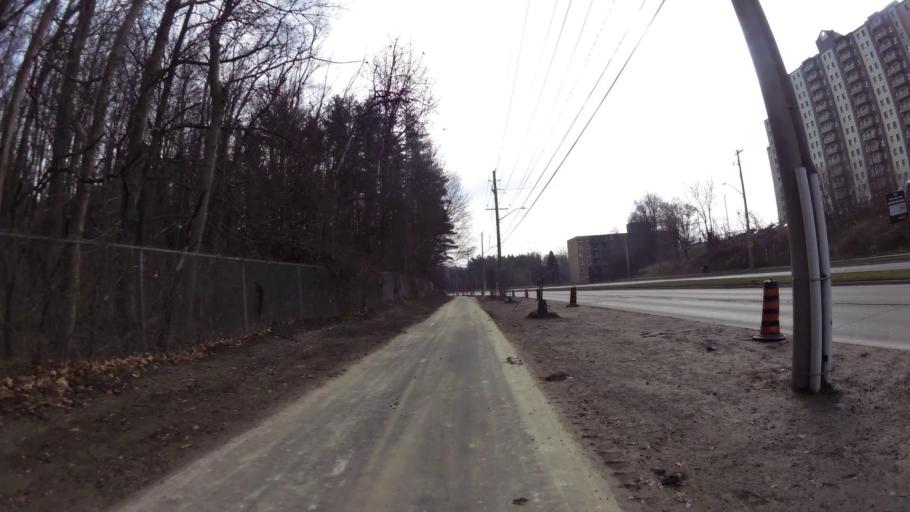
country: CA
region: Ontario
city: Kitchener
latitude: 43.3926
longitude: -80.4282
